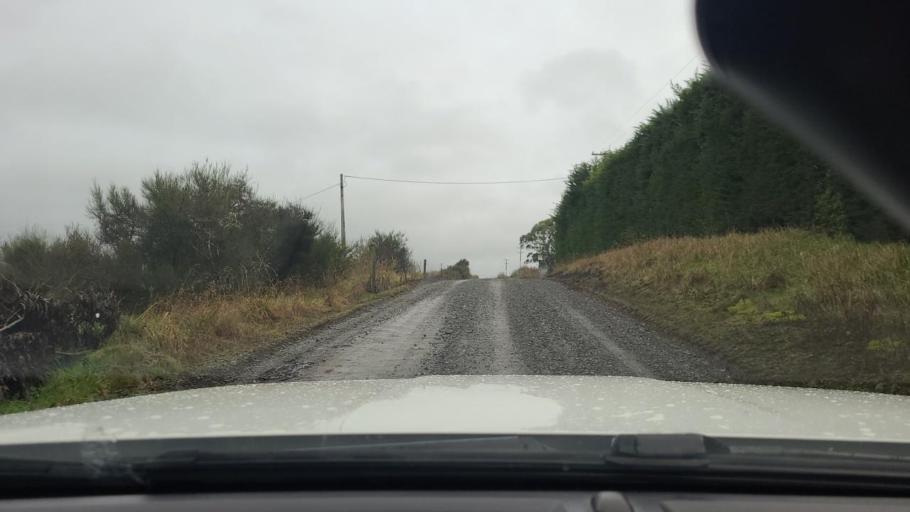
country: NZ
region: Southland
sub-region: Southland District
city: Riverton
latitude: -46.1923
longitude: 168.0399
